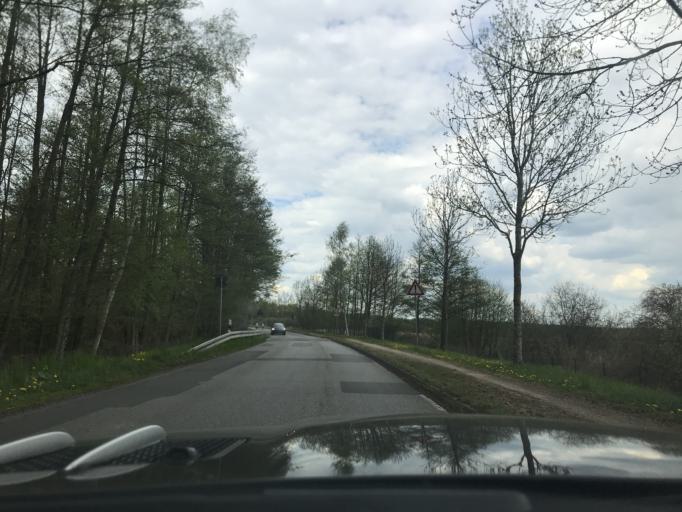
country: DE
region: Schleswig-Holstein
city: Gross Gronau
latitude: 53.7760
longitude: 10.7712
